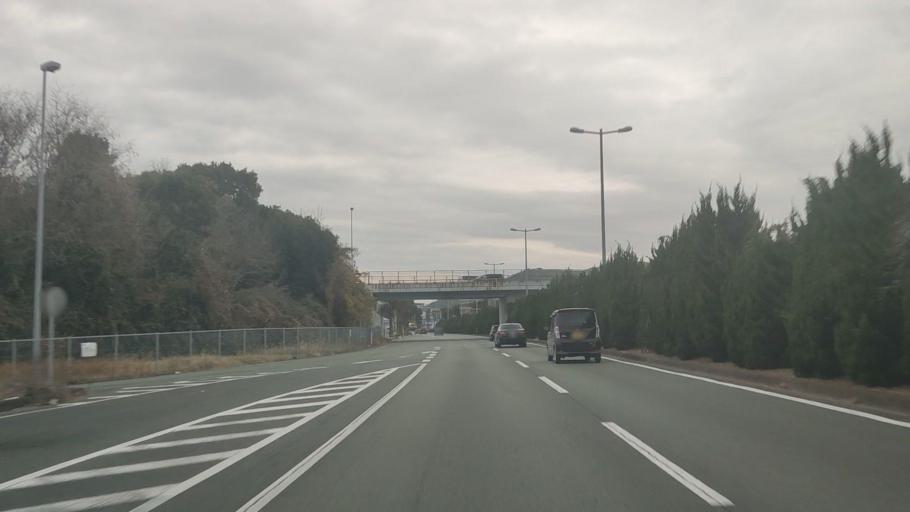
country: JP
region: Kumamoto
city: Kumamoto
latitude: 32.8328
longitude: 130.7746
